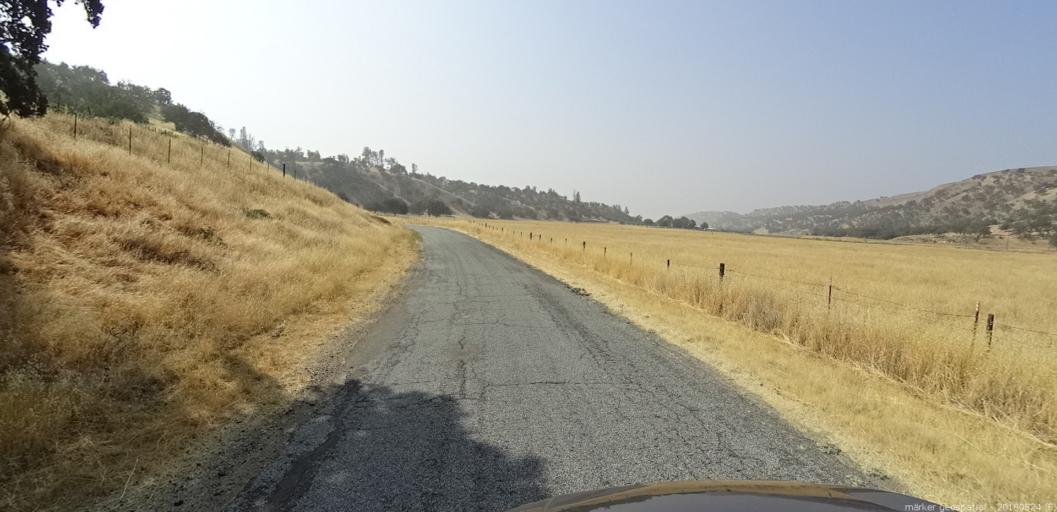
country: US
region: California
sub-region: San Luis Obispo County
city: San Miguel
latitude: 35.8812
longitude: -120.7012
